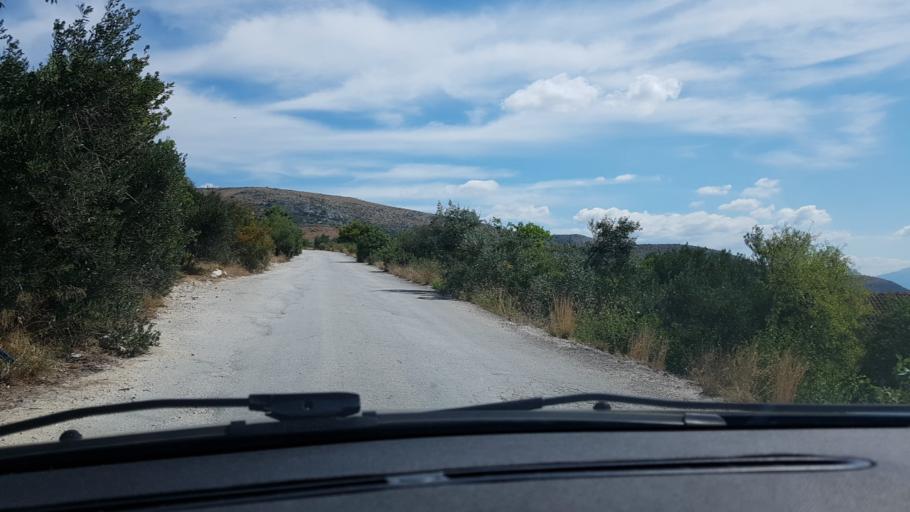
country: HR
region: Splitsko-Dalmatinska
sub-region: Grad Trogir
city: Trogir
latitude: 43.5246
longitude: 16.2266
